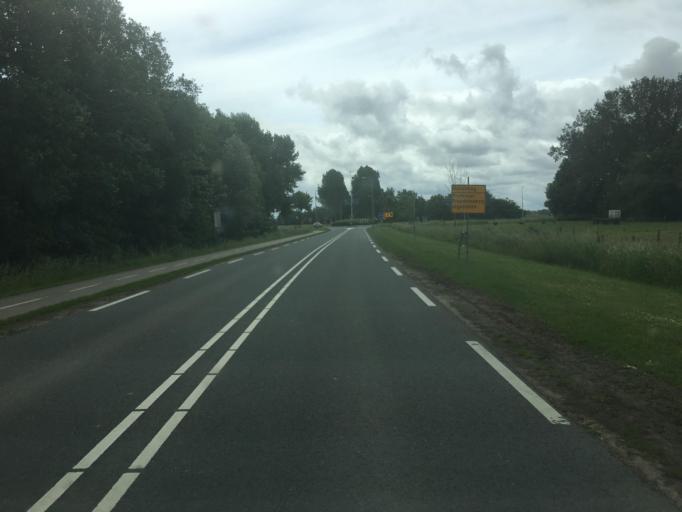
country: NL
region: Flevoland
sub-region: Gemeente Noordoostpolder
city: Emmeloord
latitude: 52.6407
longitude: 5.7225
